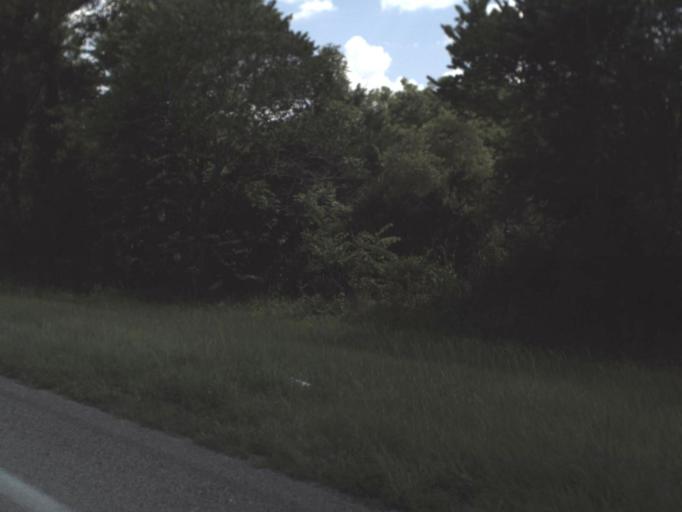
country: US
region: Florida
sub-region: Alachua County
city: Hawthorne
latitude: 29.6666
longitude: -82.1179
